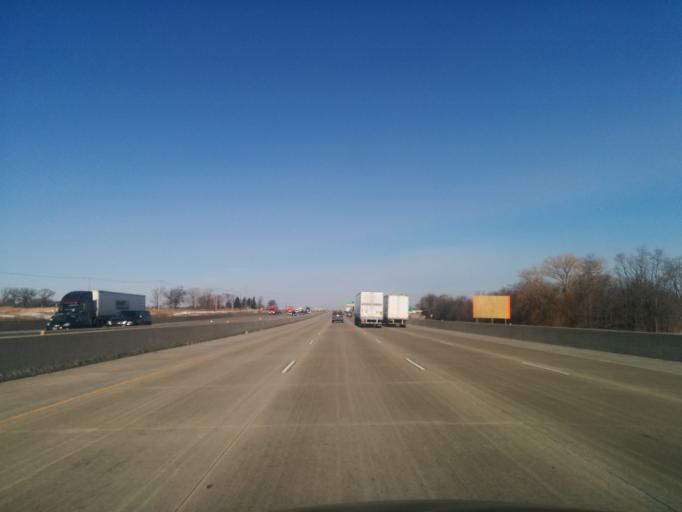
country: US
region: Wisconsin
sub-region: Kenosha County
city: Pleasant Prairie
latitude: 42.5125
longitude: -87.9515
